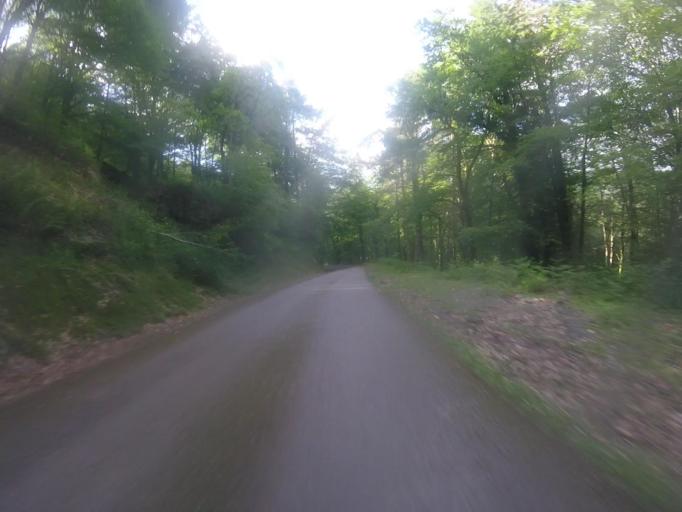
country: ES
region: Navarre
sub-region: Provincia de Navarra
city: Goizueta
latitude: 43.2336
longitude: -1.8052
